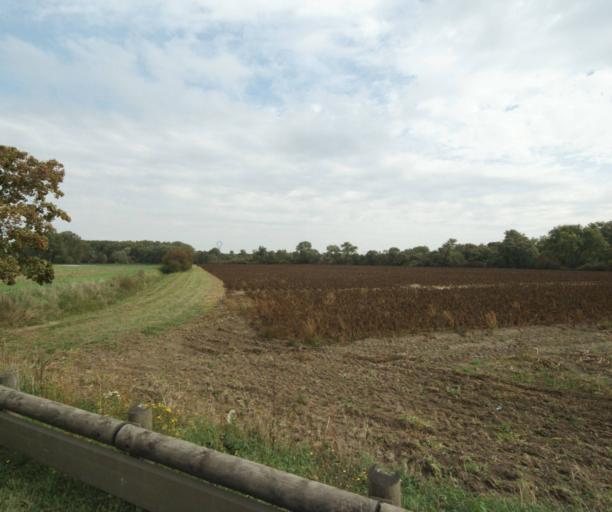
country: FR
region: Nord-Pas-de-Calais
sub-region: Departement du Pas-de-Calais
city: Billy-Berclau
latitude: 50.5350
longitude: 2.8799
